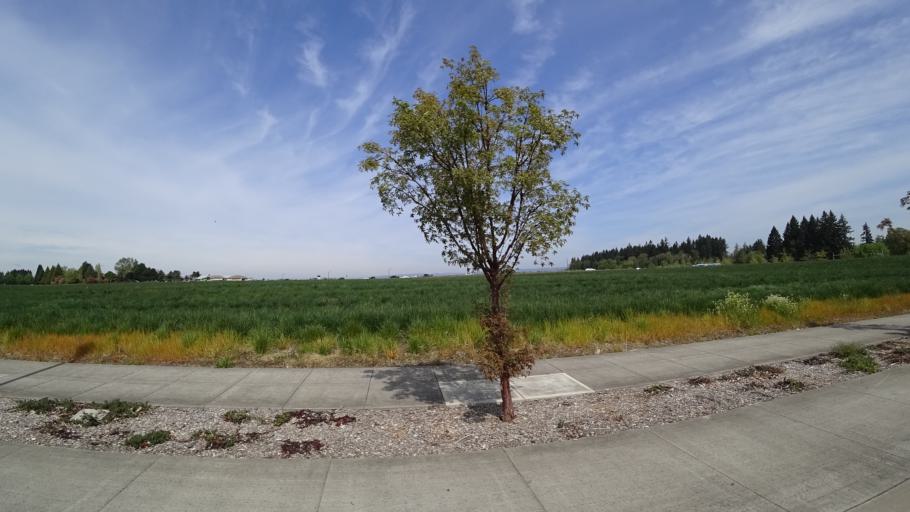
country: US
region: Oregon
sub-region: Washington County
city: Hillsboro
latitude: 45.5307
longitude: -122.9399
